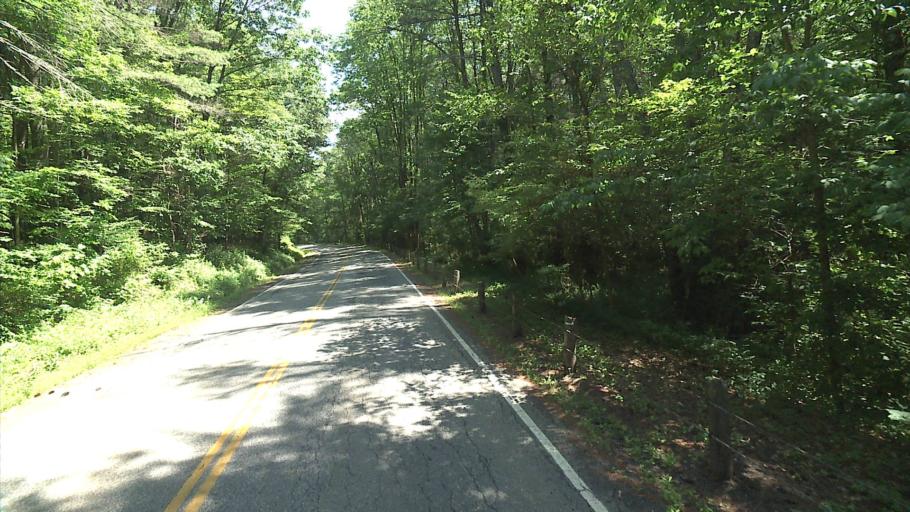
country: US
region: Connecticut
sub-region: Litchfield County
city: Canaan
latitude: 41.9102
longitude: -73.2760
